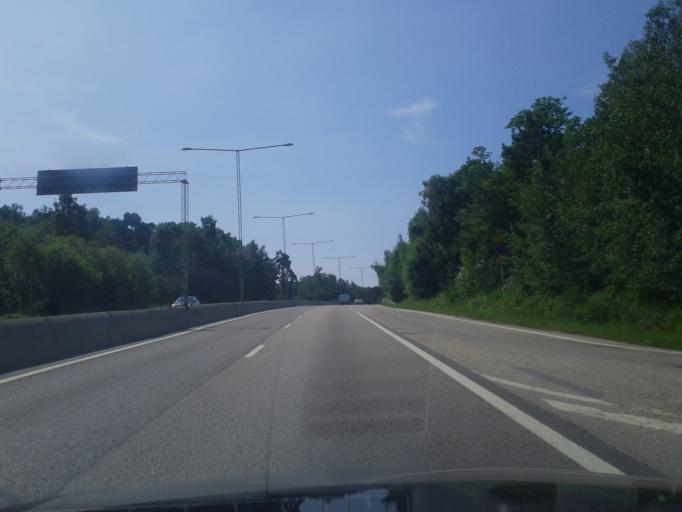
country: SE
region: Stockholm
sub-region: Huddinge Kommun
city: Huddinge
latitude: 59.2712
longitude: 18.0103
